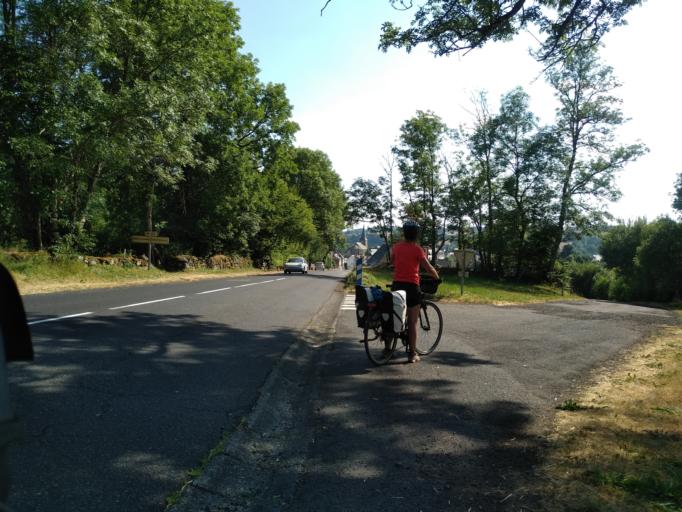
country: FR
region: Auvergne
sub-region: Departement du Cantal
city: Condat
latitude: 45.4117
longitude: 2.8314
